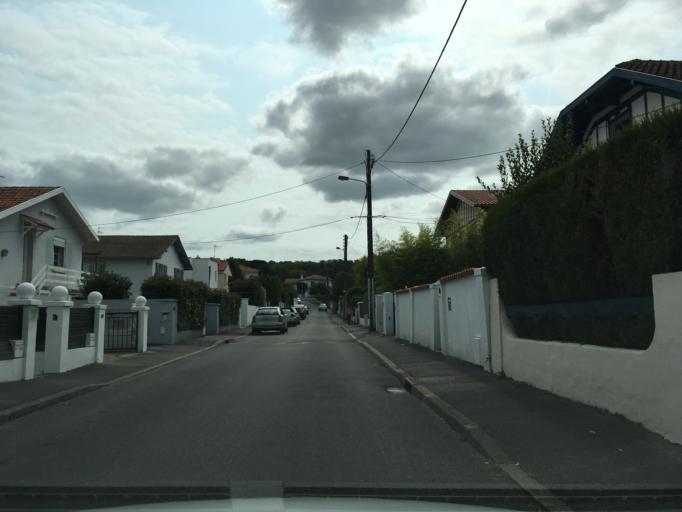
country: FR
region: Aquitaine
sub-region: Departement des Pyrenees-Atlantiques
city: Anglet
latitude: 43.4789
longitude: -1.5128
